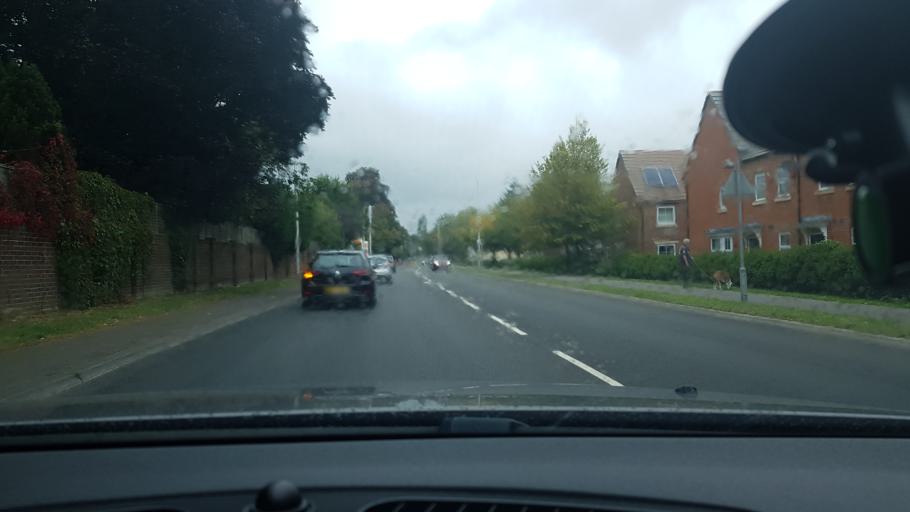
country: GB
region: England
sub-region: West Berkshire
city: Newbury
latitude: 51.4081
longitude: -1.3382
